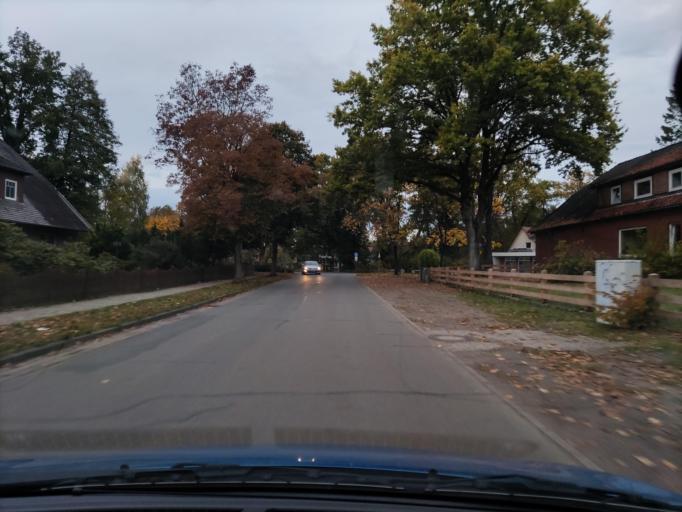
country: DE
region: Lower Saxony
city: Hermannsburg
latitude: 52.8749
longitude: 10.1204
